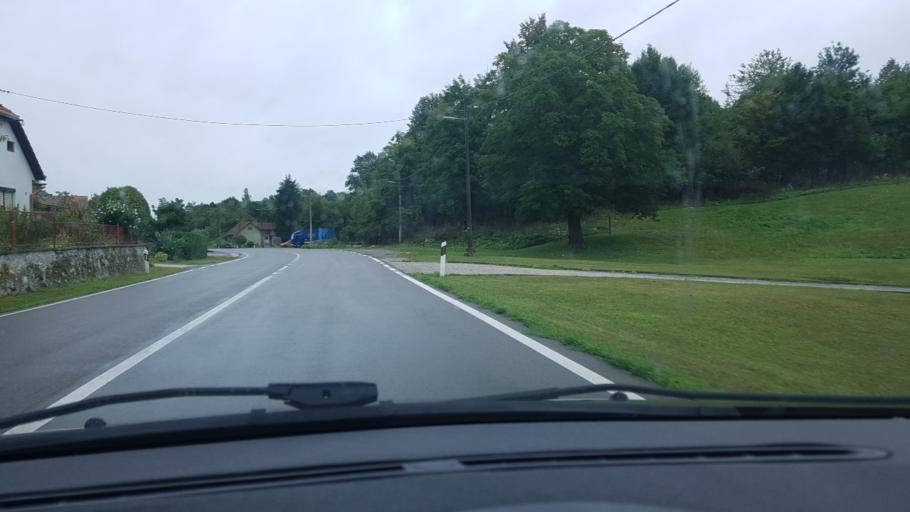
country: HR
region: Primorsko-Goranska
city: Vrbovsko
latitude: 45.4212
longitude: 15.2098
